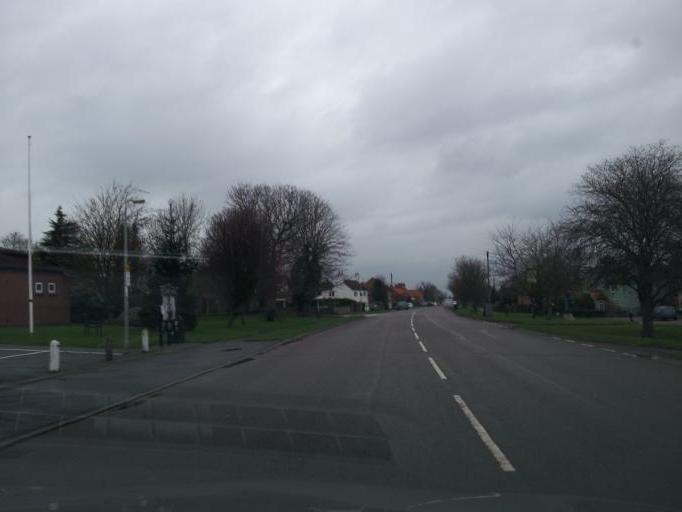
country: GB
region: England
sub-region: Lincolnshire
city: Long Bennington
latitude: 52.9943
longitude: -0.7587
